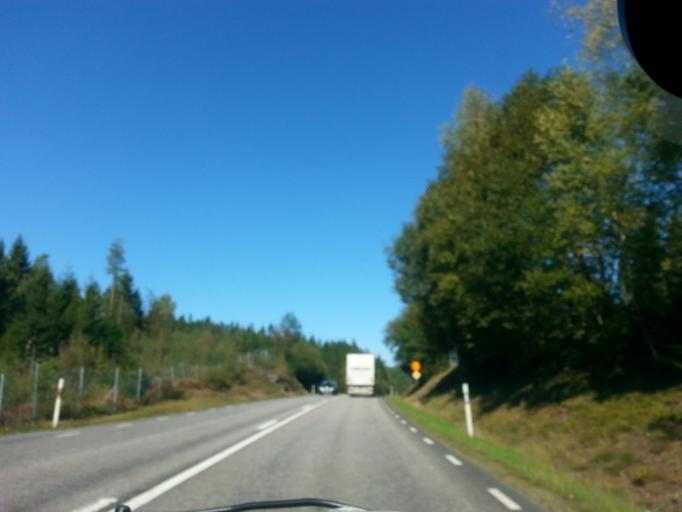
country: SE
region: Vaestra Goetaland
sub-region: Harryda Kommun
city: Ravlanda
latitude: 57.5718
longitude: 12.5074
